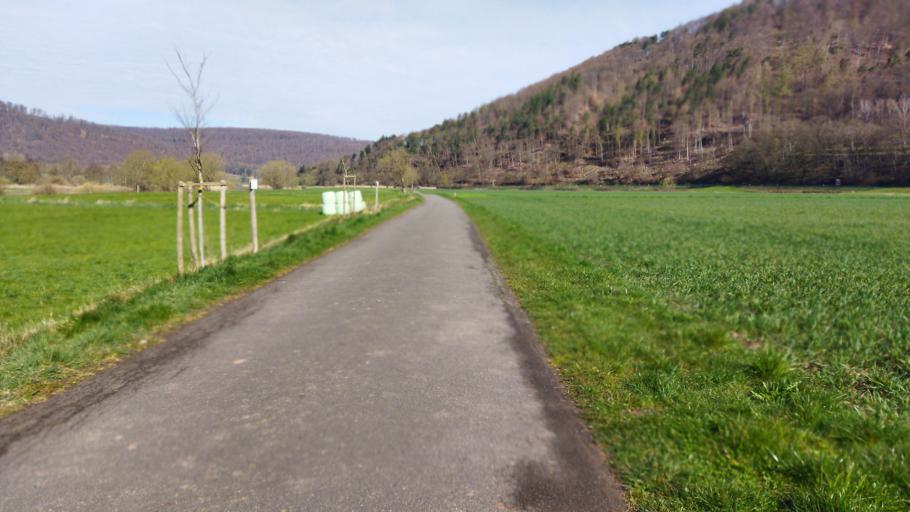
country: DE
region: Lower Saxony
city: Buhren
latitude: 51.5051
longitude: 9.6018
